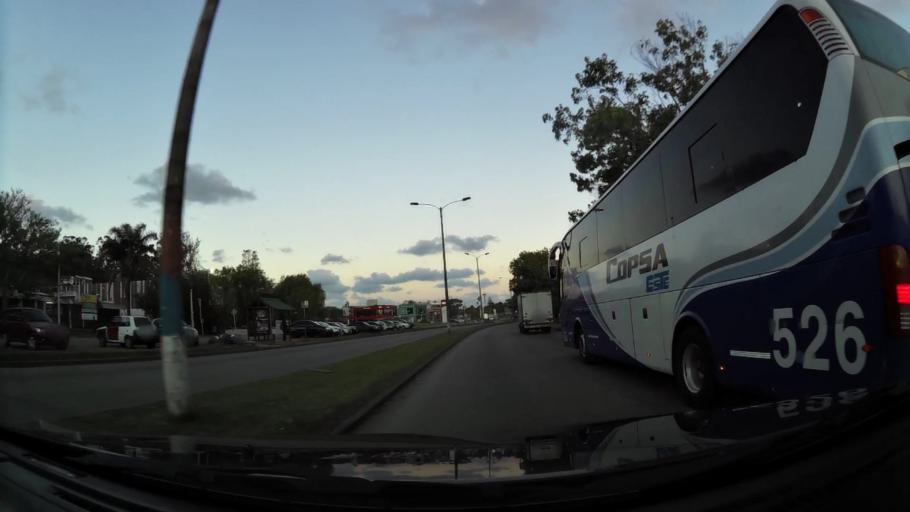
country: UY
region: Canelones
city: Paso de Carrasco
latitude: -34.8836
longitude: -56.0906
